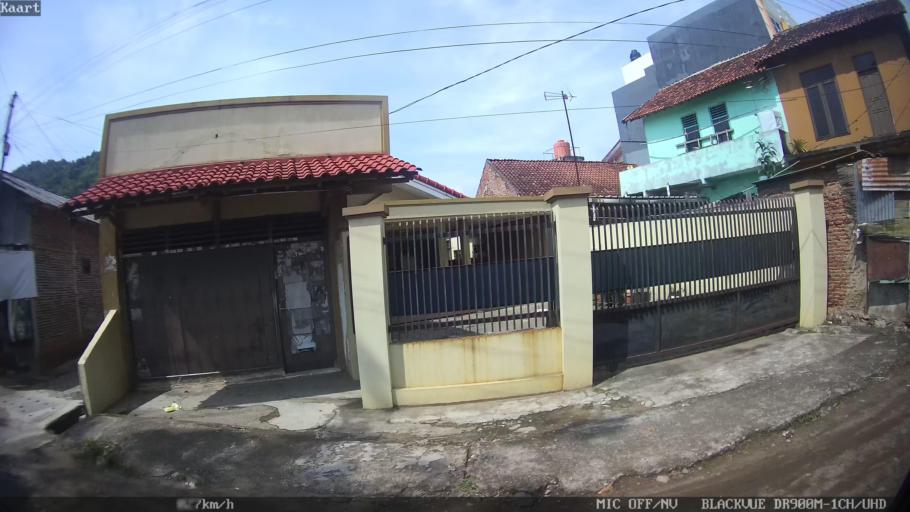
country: ID
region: Lampung
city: Kedaton
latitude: -5.3872
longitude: 105.2678
